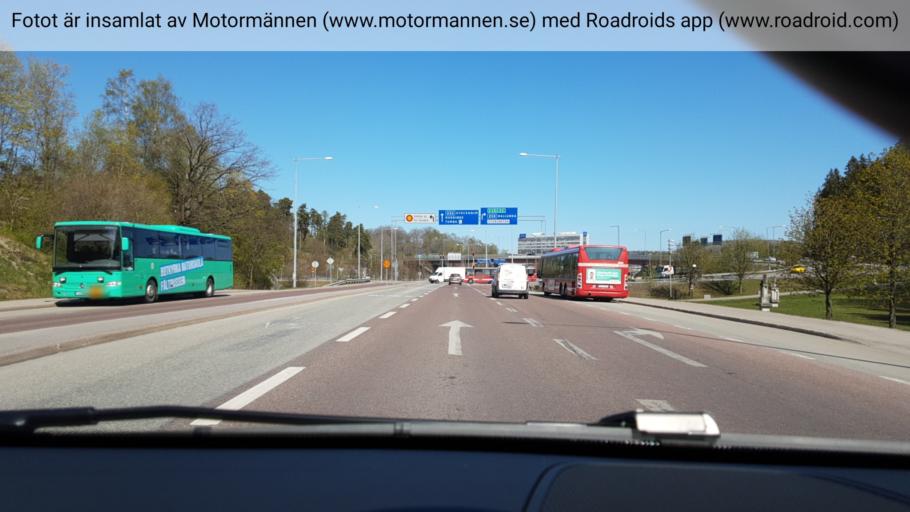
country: SE
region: Stockholm
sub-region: Botkyrka Kommun
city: Tumba
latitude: 59.1972
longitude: 17.8365
